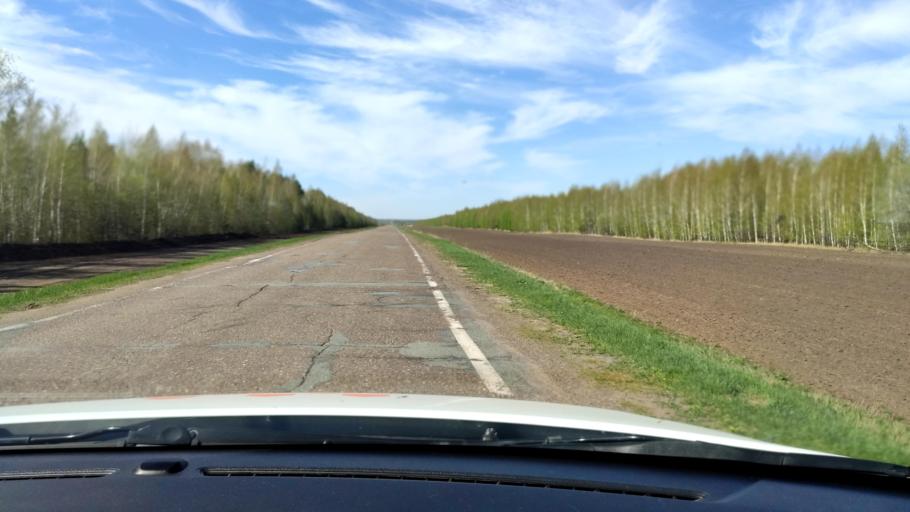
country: RU
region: Tatarstan
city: Stolbishchi
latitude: 55.5412
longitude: 49.2296
